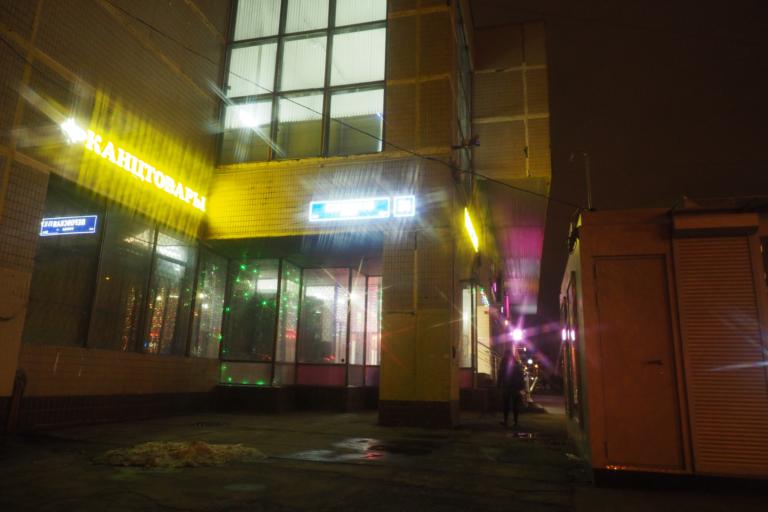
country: RU
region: Moscow
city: Ryazanskiy
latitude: 55.7468
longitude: 37.7747
